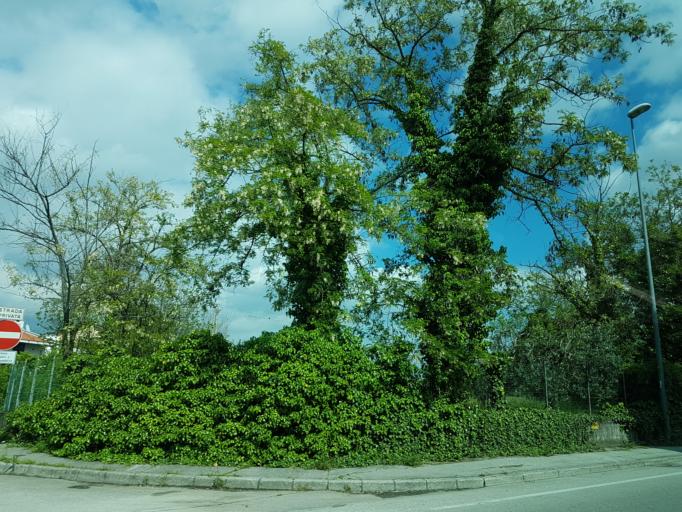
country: IT
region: Veneto
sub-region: Provincia di Vicenza
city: Bassano del Grappa
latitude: 45.7559
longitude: 11.7439
